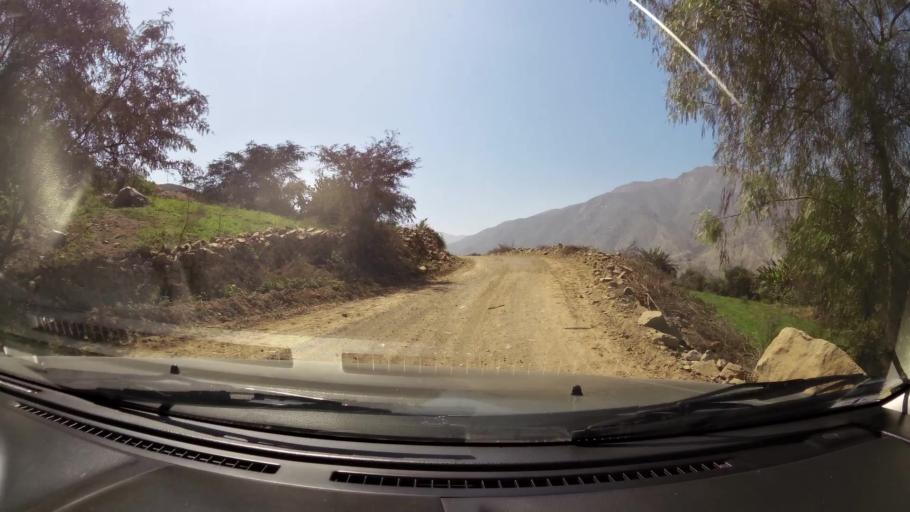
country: PE
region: Ica
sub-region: Provincia de Ica
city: Guadalupe
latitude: -13.8726
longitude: -75.6398
